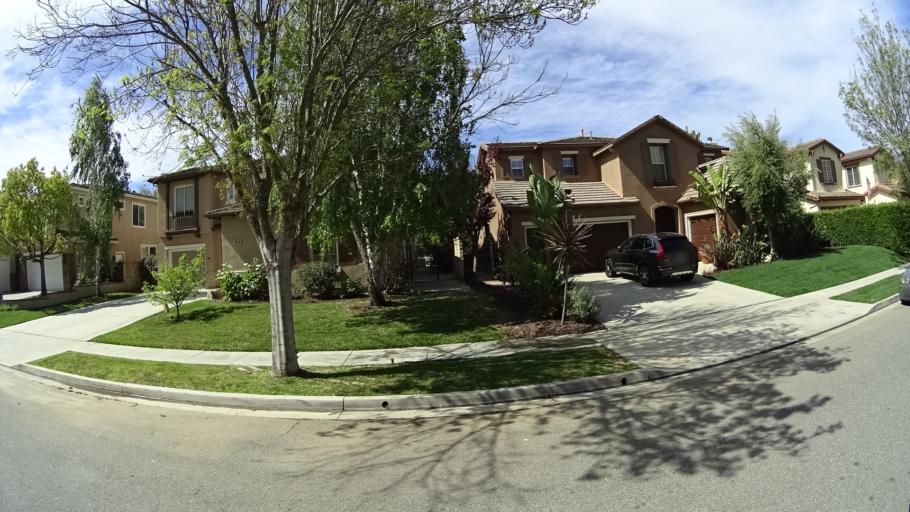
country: US
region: California
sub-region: Ventura County
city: Casa Conejo
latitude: 34.1725
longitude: -118.9781
